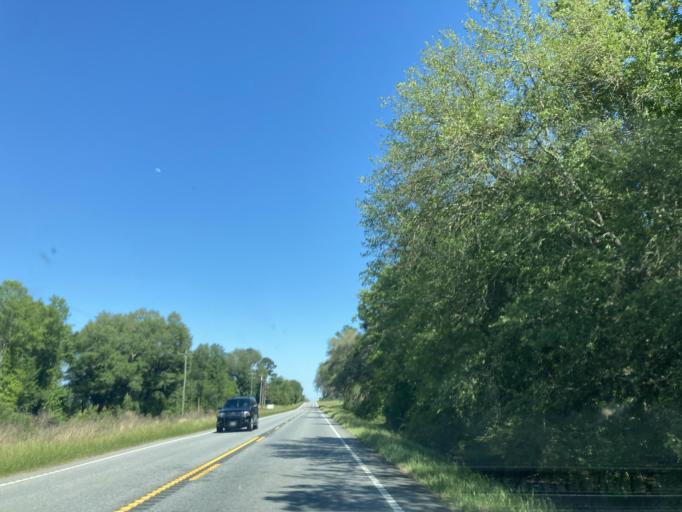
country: US
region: Georgia
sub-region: Miller County
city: Colquitt
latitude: 31.1846
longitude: -84.5811
